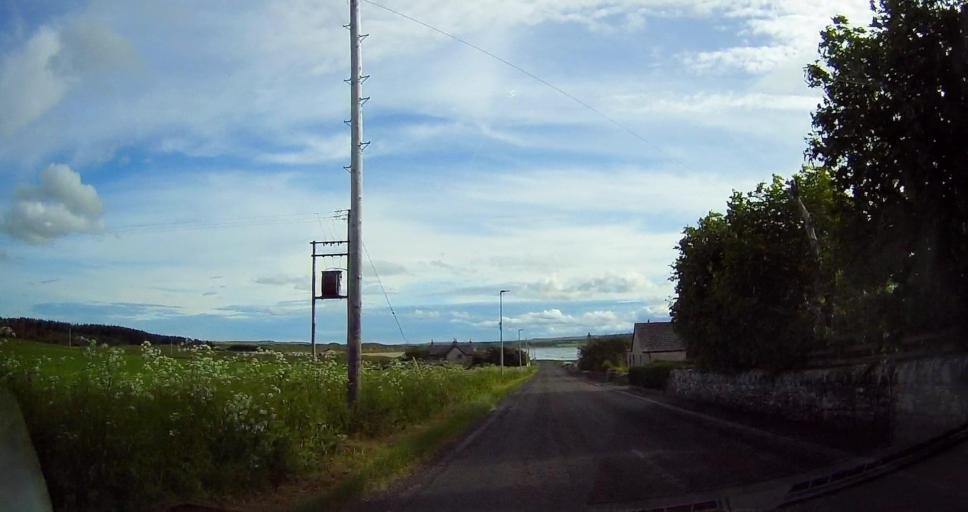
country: GB
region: Scotland
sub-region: Highland
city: Thurso
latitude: 58.6211
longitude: -3.3439
